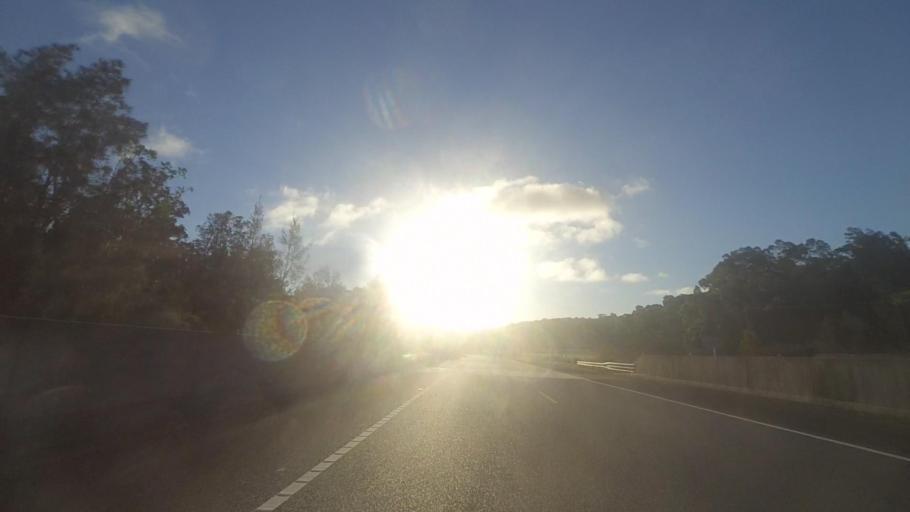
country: AU
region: New South Wales
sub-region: Great Lakes
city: Hawks Nest
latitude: -32.5477
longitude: 152.1582
